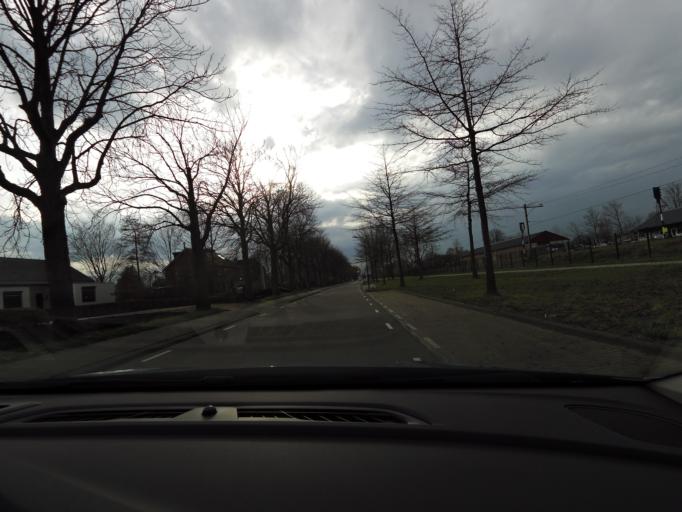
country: NL
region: South Holland
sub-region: Gemeente Hardinxveld-Giessendam
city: Neder-Hardinxveld
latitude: 51.8311
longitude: 4.8583
